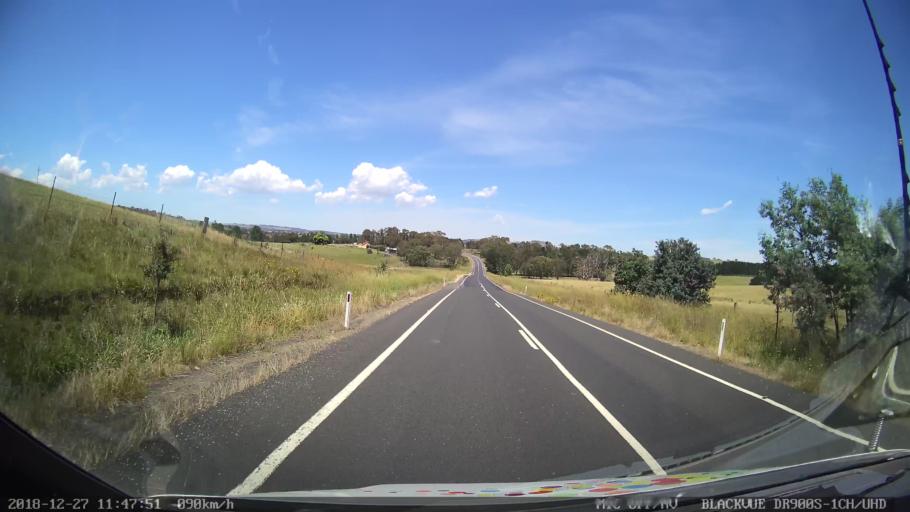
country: AU
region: New South Wales
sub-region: Bathurst Regional
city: Perthville
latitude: -33.5996
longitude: 149.4402
